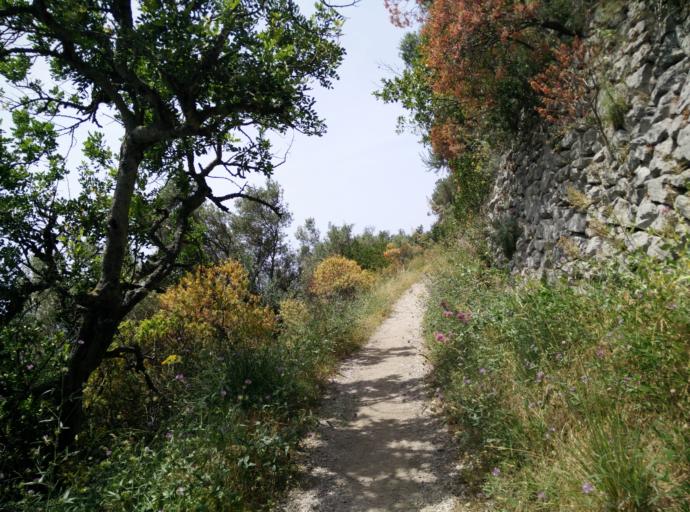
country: IT
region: Campania
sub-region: Provincia di Napoli
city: Massa Lubrense
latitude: 40.5817
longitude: 14.3477
